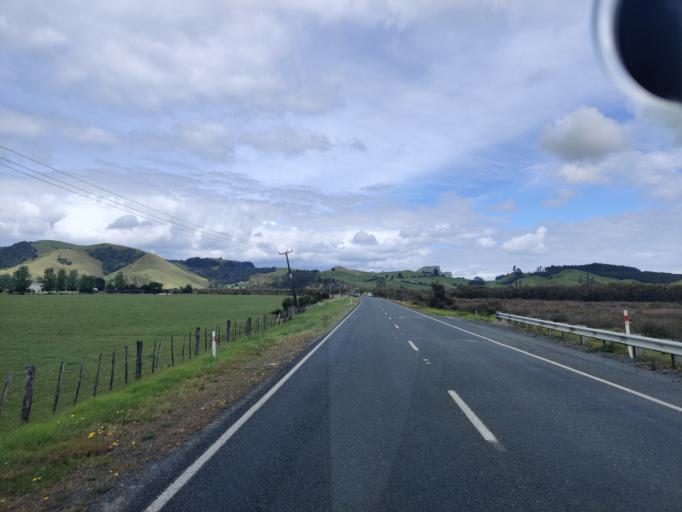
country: NZ
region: Northland
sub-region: Far North District
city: Kerikeri
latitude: -35.0847
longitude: 173.7273
